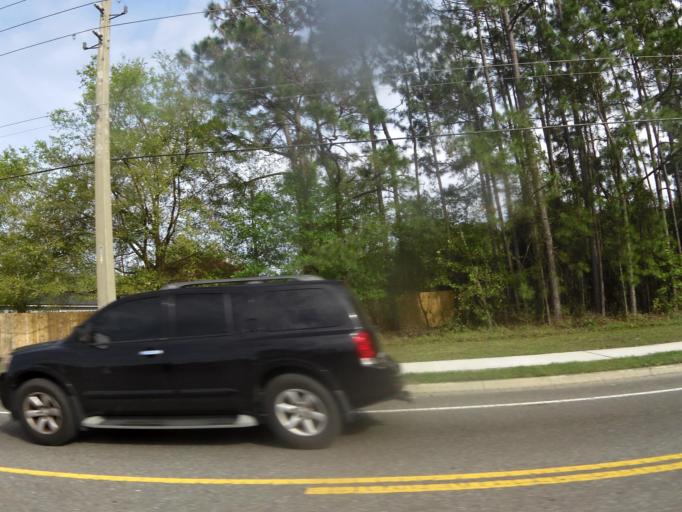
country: US
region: Florida
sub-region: Clay County
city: Bellair-Meadowbrook Terrace
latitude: 30.2568
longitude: -81.7856
